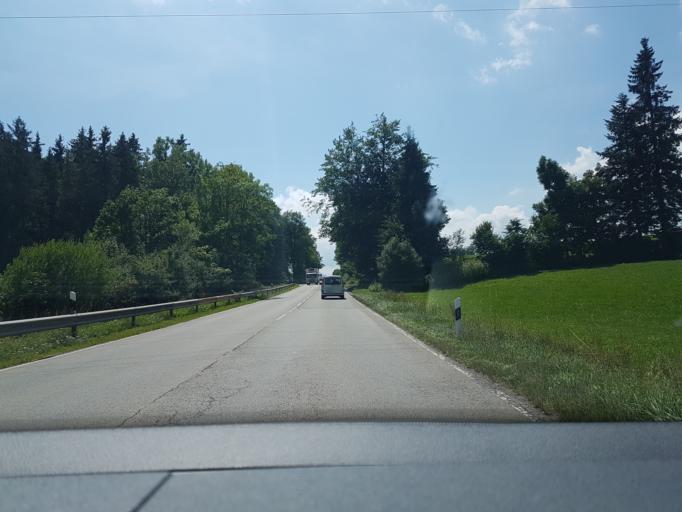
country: DE
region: Bavaria
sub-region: Upper Bavaria
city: Miesbach
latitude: 47.8107
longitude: 11.8386
